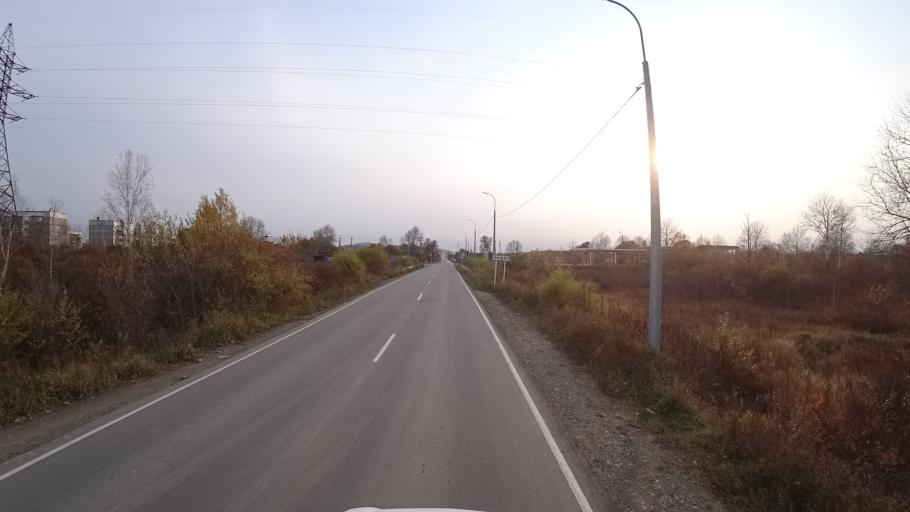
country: RU
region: Khabarovsk Krai
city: Amursk
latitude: 50.1065
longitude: 136.5140
